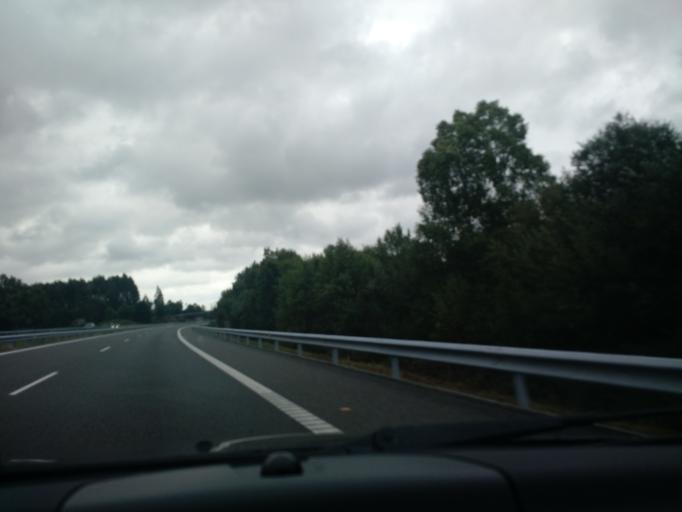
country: ES
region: Galicia
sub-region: Provincia da Coruna
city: Ordes
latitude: 43.0311
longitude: -8.3989
